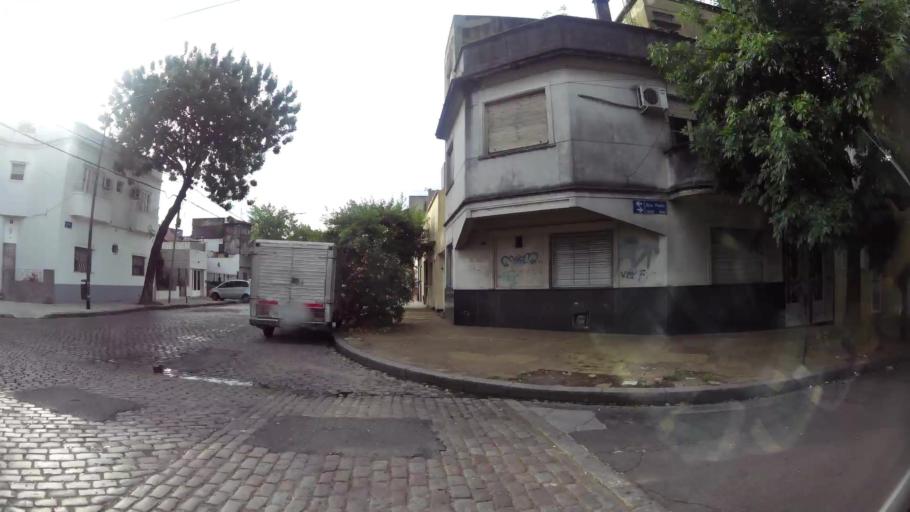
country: AR
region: Buenos Aires F.D.
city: Villa Santa Rita
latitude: -34.6435
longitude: -58.4748
